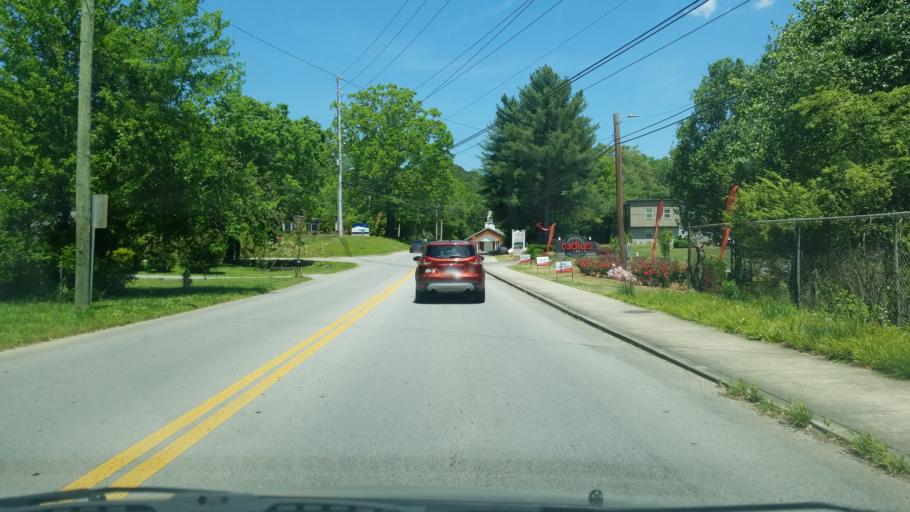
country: US
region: Tennessee
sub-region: Hamilton County
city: Signal Mountain
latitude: 35.1061
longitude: -85.3266
